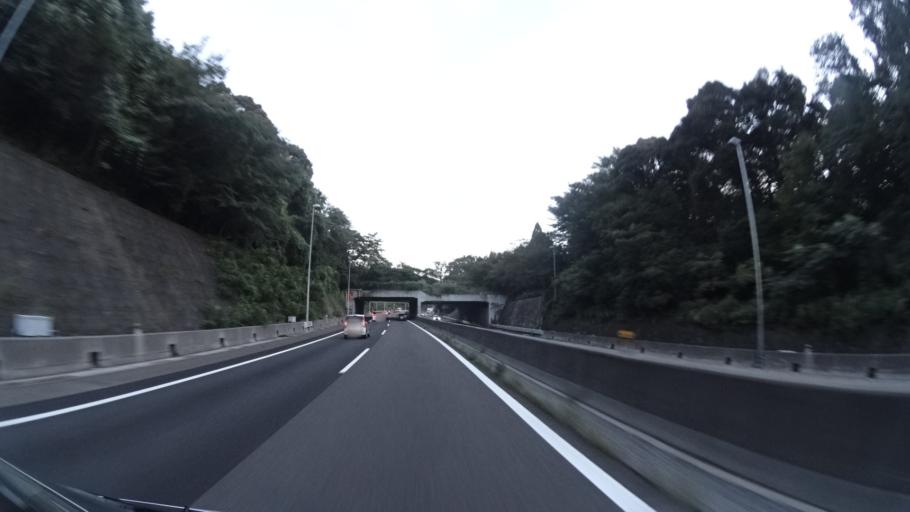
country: JP
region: Shiga Prefecture
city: Hikone
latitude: 35.1855
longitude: 136.2816
